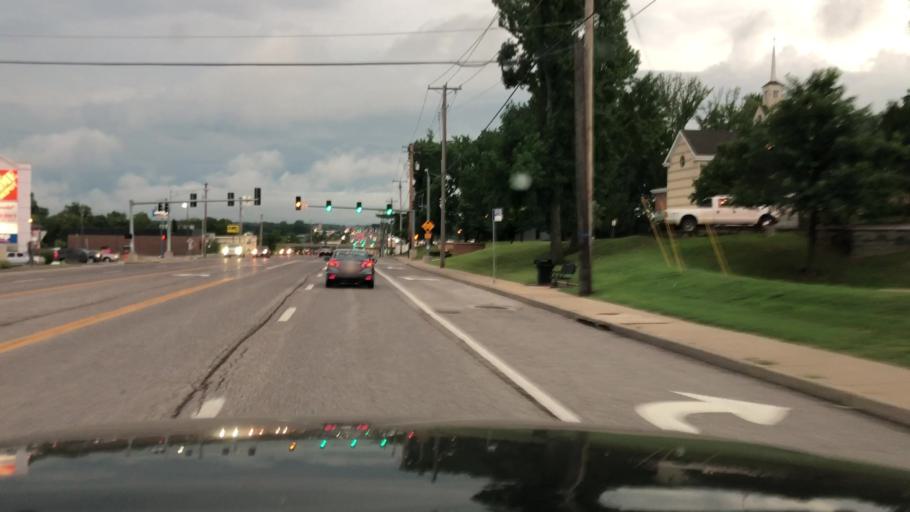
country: US
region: Missouri
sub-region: Saint Louis County
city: Saint Ann
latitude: 38.7397
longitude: -90.4026
